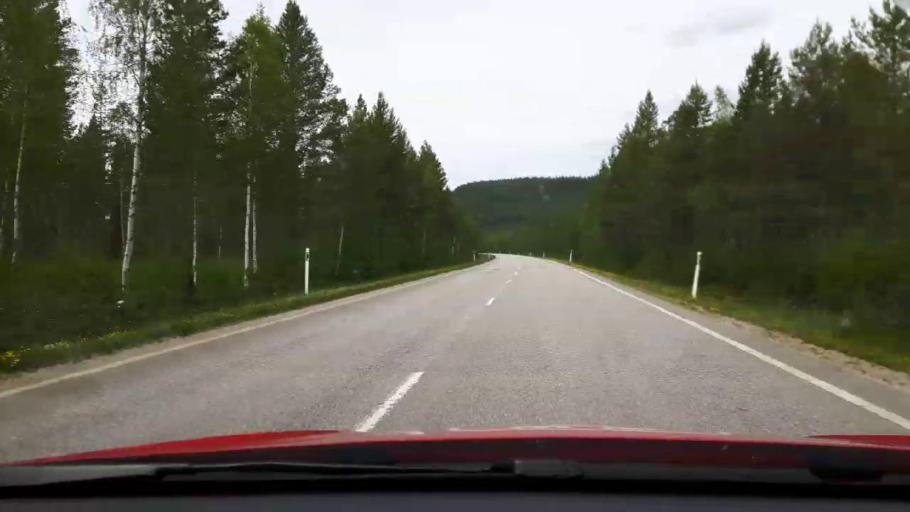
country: SE
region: Jaemtland
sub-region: Harjedalens Kommun
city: Sveg
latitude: 62.0928
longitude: 14.2414
